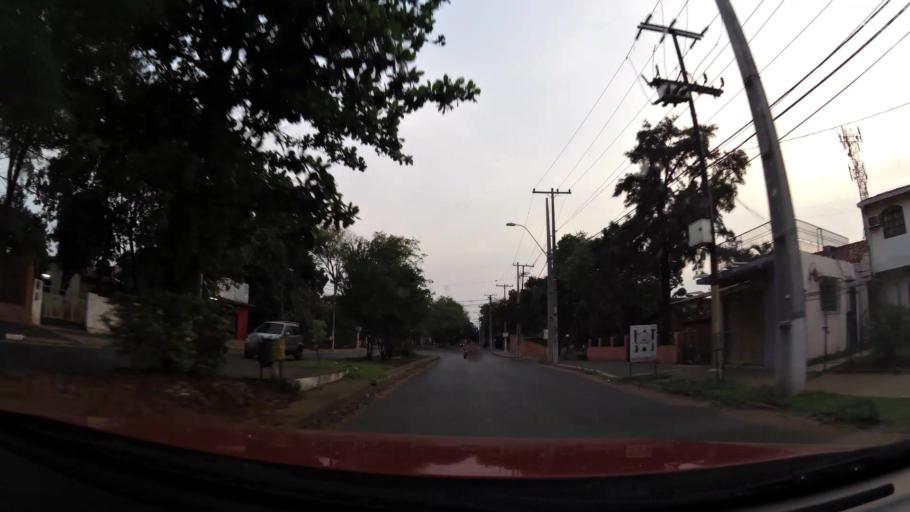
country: PY
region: Central
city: Lambare
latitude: -25.3305
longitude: -57.6193
